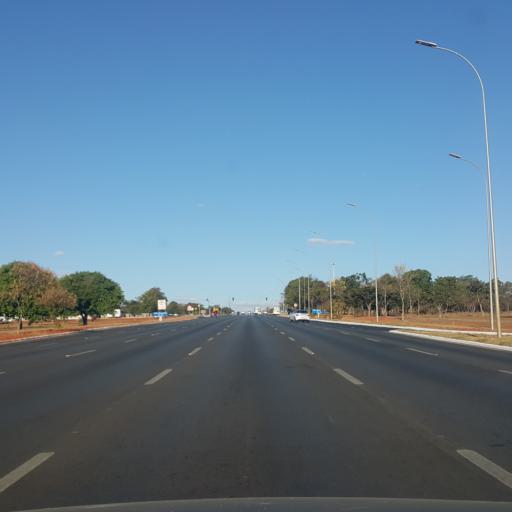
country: BR
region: Federal District
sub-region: Brasilia
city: Brasilia
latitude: -15.7807
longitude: -47.9277
